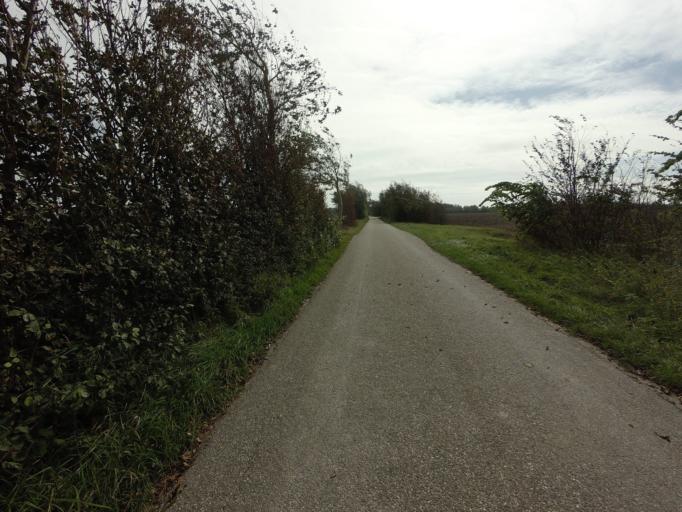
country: NL
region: Zeeland
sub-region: Gemeente Vlissingen
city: Vlissingen
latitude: 51.5286
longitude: 3.4673
